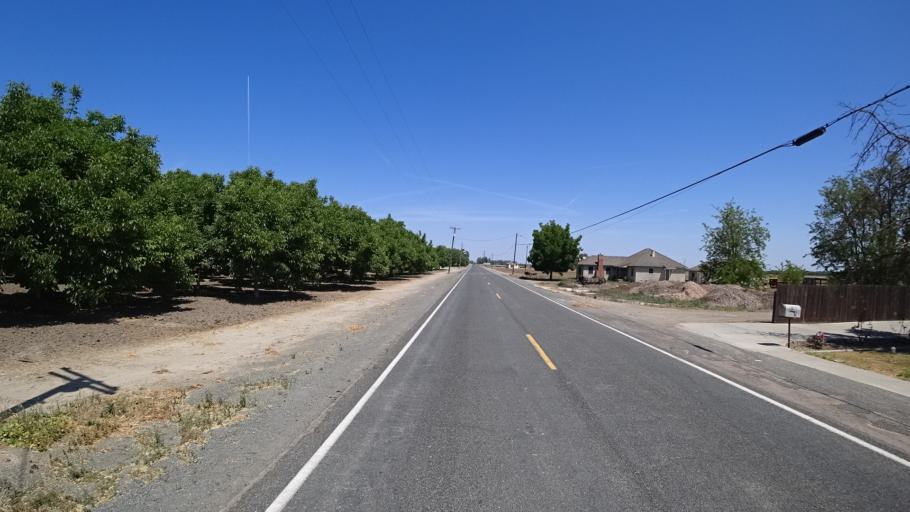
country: US
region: California
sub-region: Kings County
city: Armona
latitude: 36.2452
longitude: -119.7090
